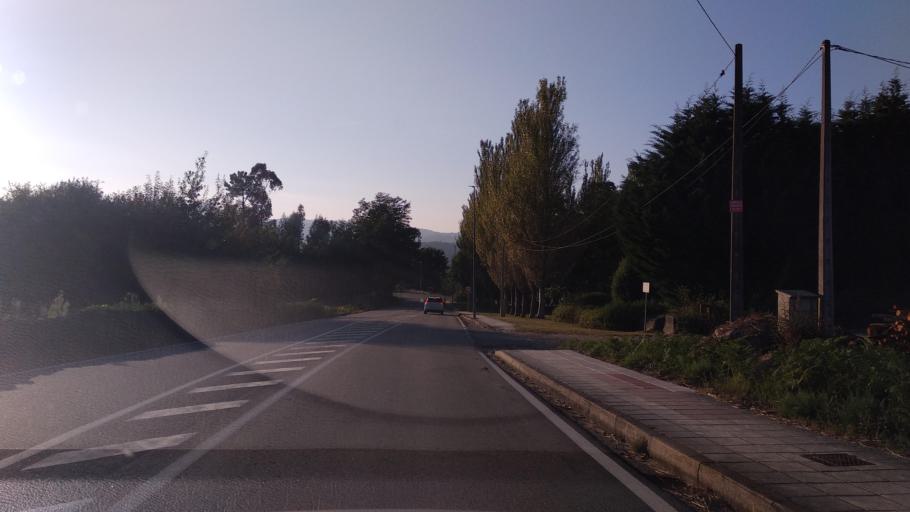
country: ES
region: Galicia
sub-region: Provincia de Pontevedra
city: Redondela
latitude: 42.3403
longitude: -8.5917
